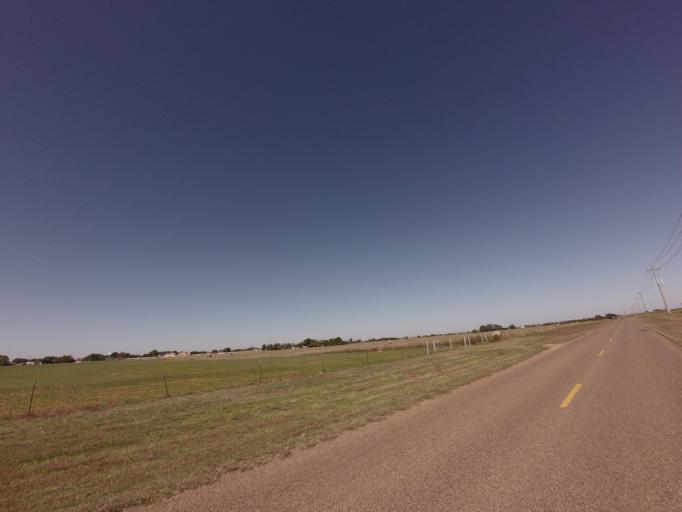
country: US
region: New Mexico
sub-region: Curry County
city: Clovis
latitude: 34.4292
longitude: -103.1608
